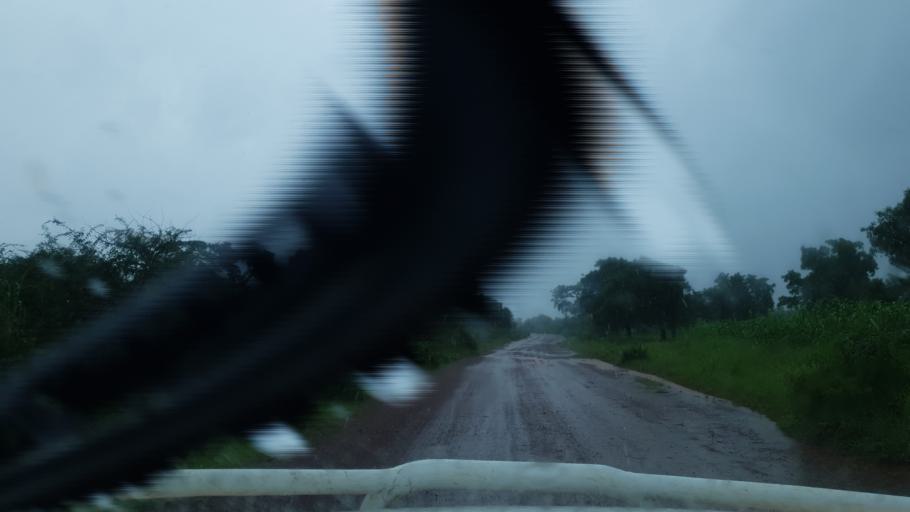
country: ML
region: Sikasso
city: Kolondieba
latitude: 11.6086
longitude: -6.6752
